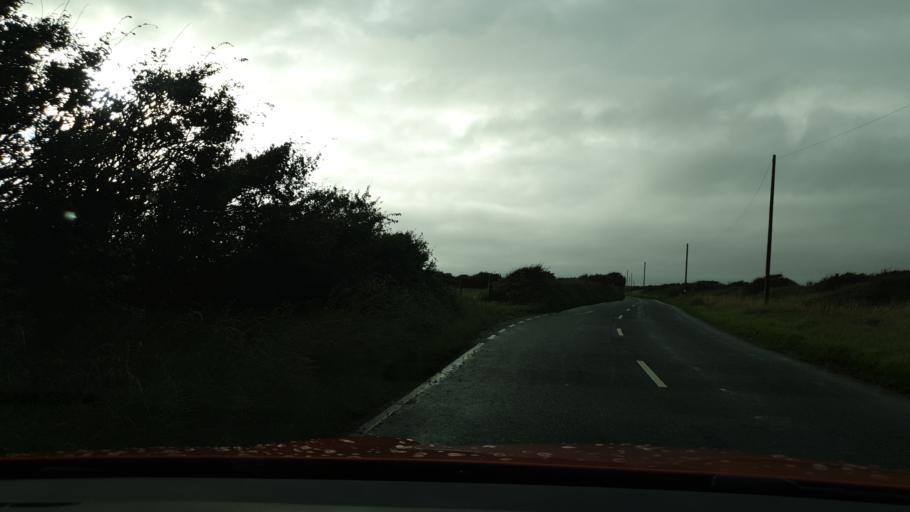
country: GB
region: England
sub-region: Cumbria
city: Barrow in Furness
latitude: 54.0888
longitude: -3.2435
